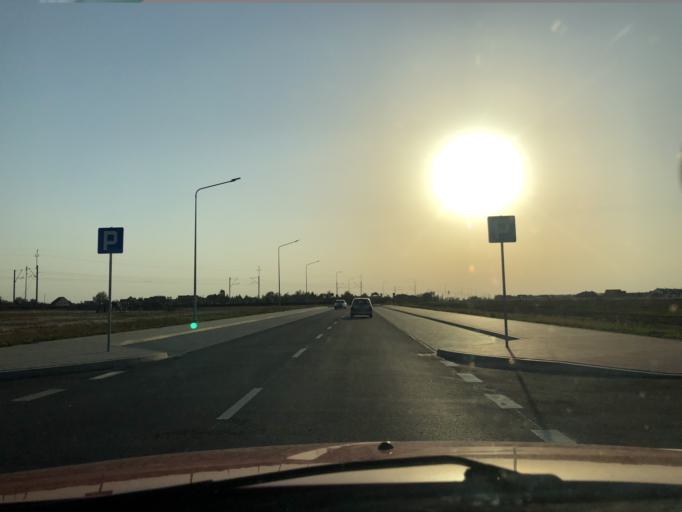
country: PL
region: Greater Poland Voivodeship
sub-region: Powiat poznanski
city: Dopiewo
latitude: 52.3751
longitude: 16.7370
